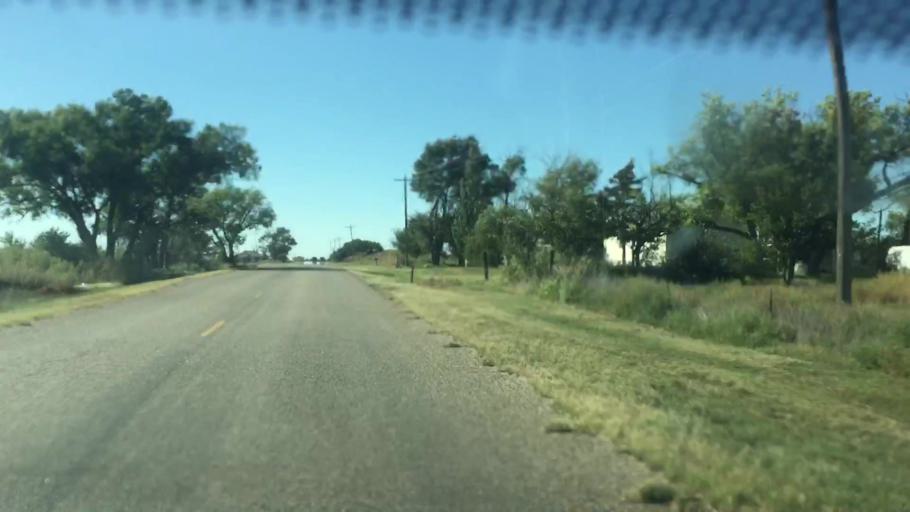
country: US
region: Colorado
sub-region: Prowers County
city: Lamar
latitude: 38.1157
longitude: -102.5893
